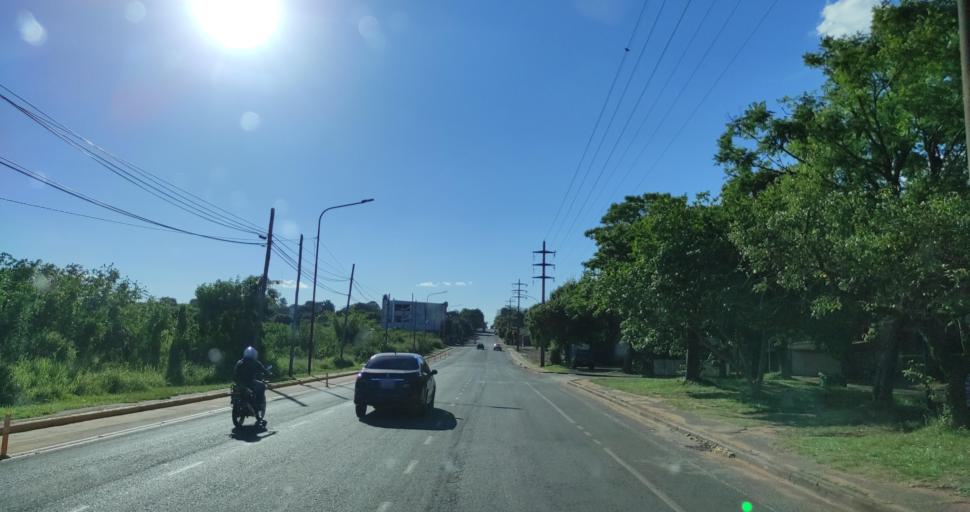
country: AR
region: Misiones
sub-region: Departamento de Capital
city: Posadas
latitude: -27.3735
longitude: -55.9341
